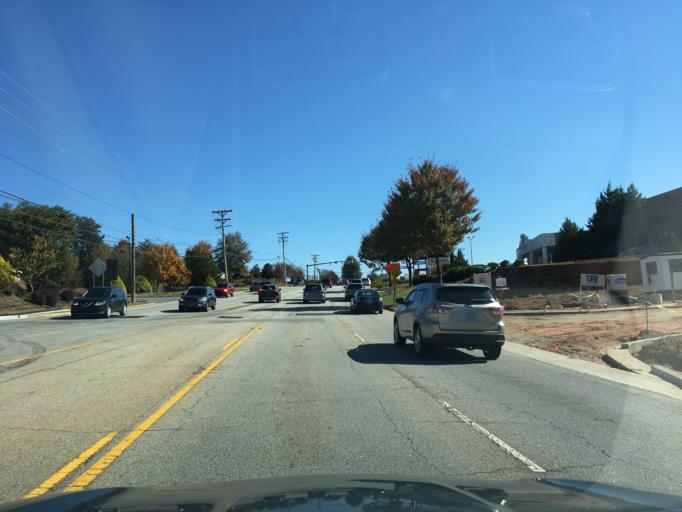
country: US
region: South Carolina
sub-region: Greenville County
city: Mauldin
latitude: 34.8362
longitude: -82.3144
